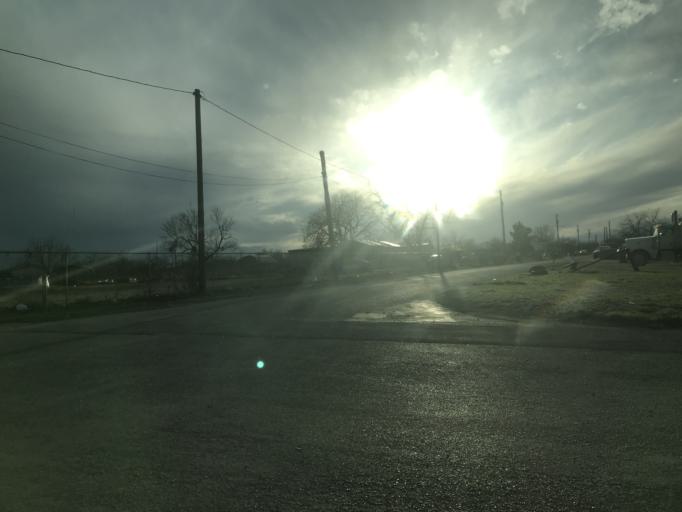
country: US
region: Texas
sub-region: Tom Green County
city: San Angelo
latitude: 31.4955
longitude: -100.4426
